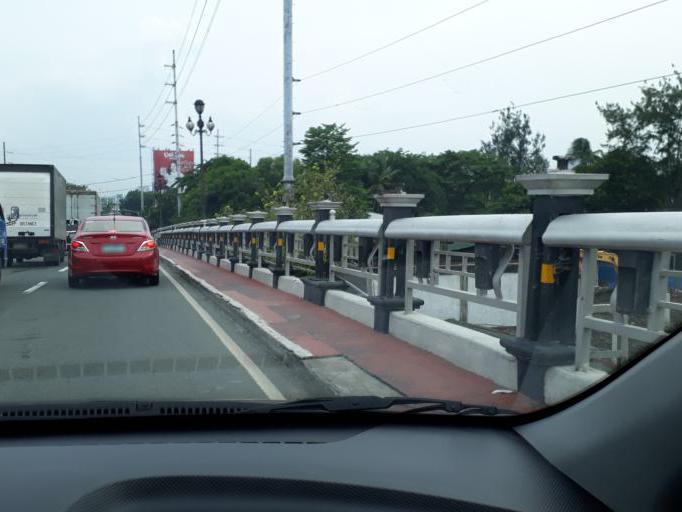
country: PH
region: Metro Manila
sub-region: City of Manila
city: Quiapo
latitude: 14.5950
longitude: 121.0015
